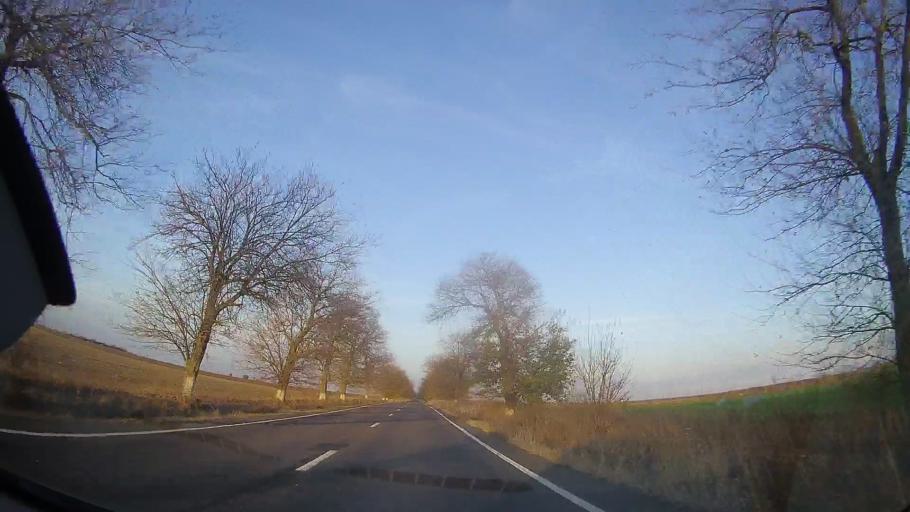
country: RO
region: Constanta
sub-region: Comuna Amzacea
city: Amzacea
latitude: 43.9495
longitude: 28.3809
